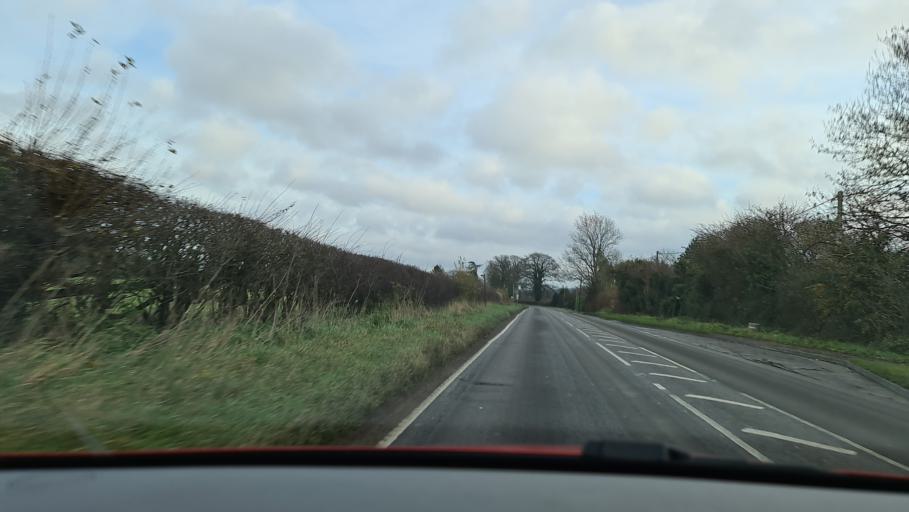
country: GB
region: England
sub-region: Buckinghamshire
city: Weston Turville
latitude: 51.7618
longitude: -0.7930
